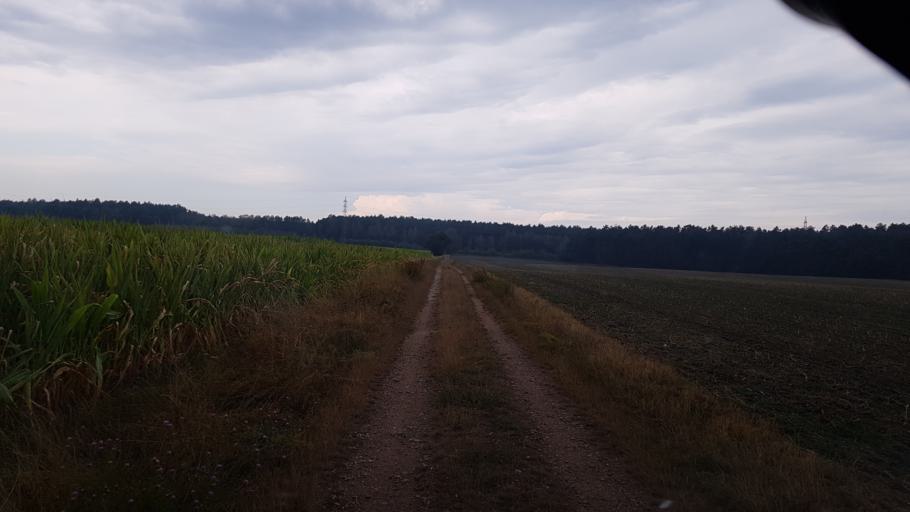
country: DE
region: Brandenburg
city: Finsterwalde
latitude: 51.6347
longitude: 13.7626
